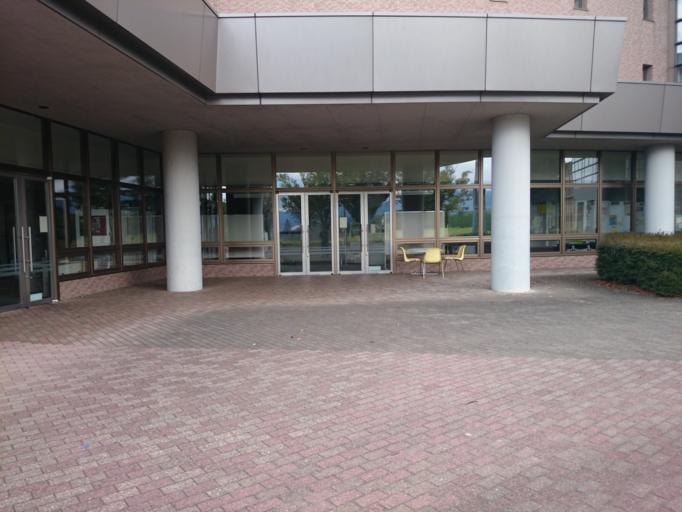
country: JP
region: Iwate
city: Morioka-shi
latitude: 39.8014
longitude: 141.1377
